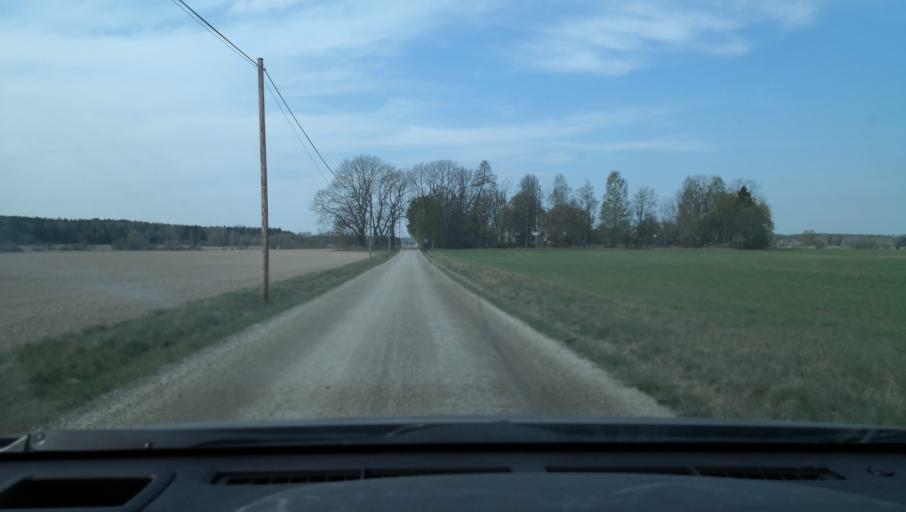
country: SE
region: Vaestmanland
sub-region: Vasteras
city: Skultuna
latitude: 59.7901
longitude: 16.4494
